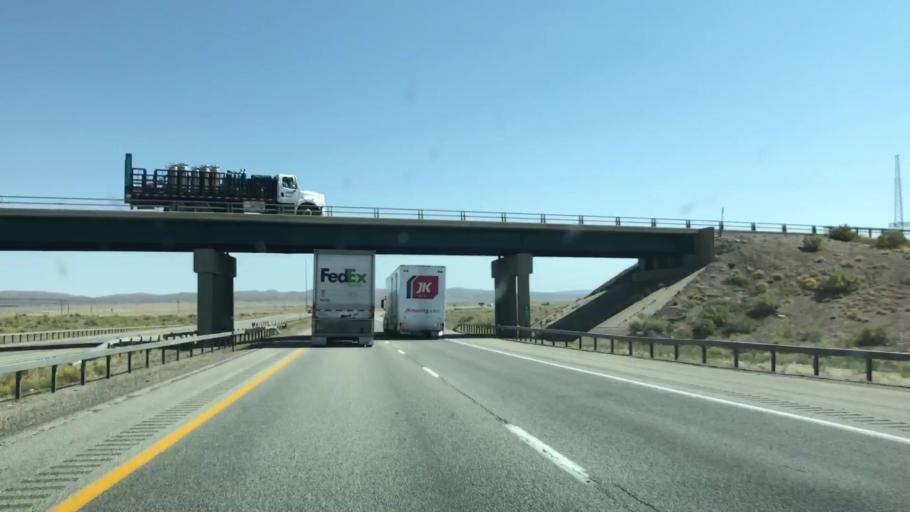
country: US
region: Wyoming
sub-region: Carbon County
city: Rawlins
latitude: 41.7718
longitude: -107.0797
